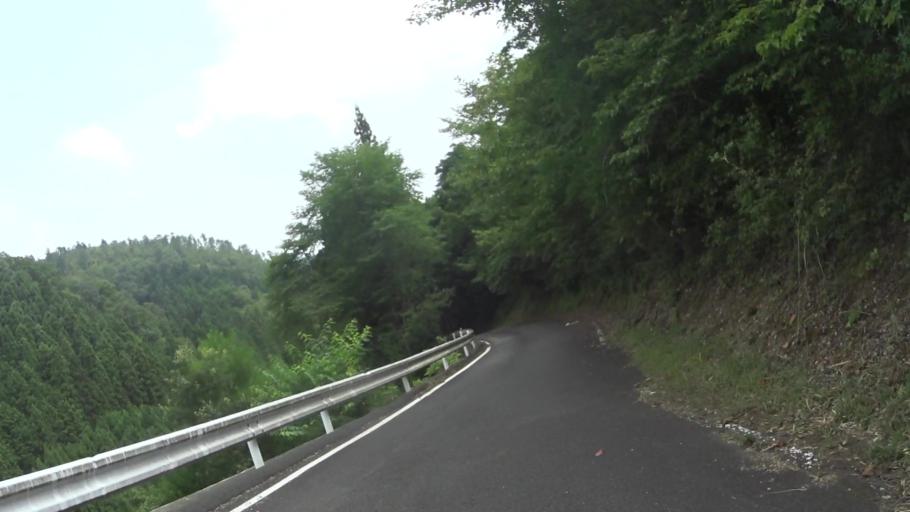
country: JP
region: Kyoto
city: Kameoka
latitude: 35.2030
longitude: 135.5827
